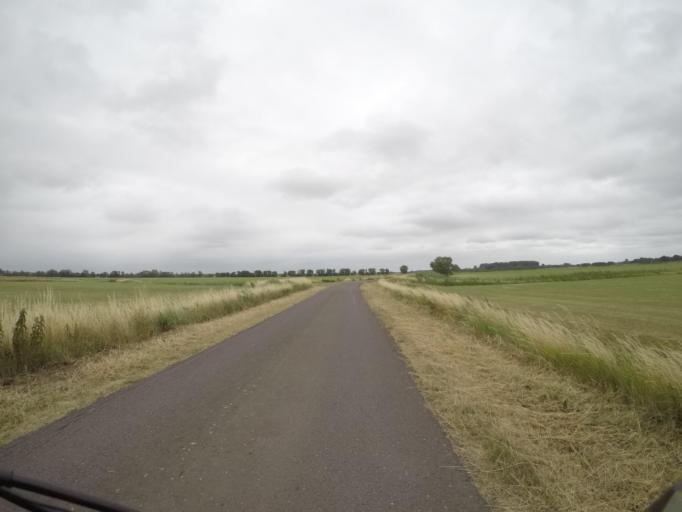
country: DE
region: Lower Saxony
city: Hitzacker
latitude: 53.1719
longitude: 11.0903
